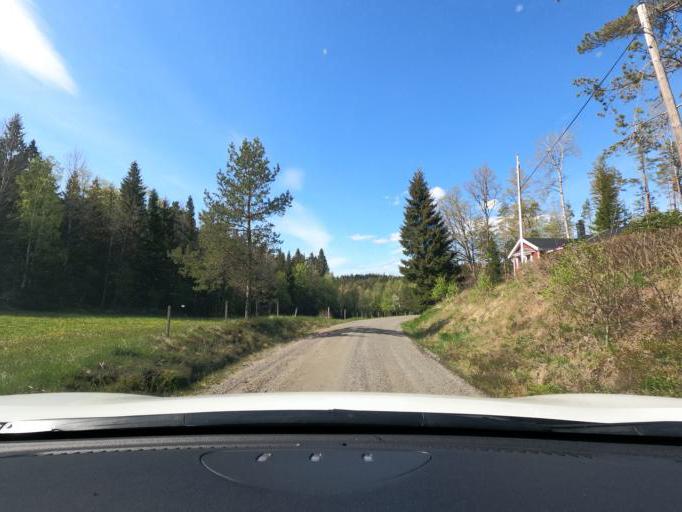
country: SE
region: Vaestra Goetaland
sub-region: Harryda Kommun
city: Ravlanda
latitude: 57.5844
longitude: 12.4932
